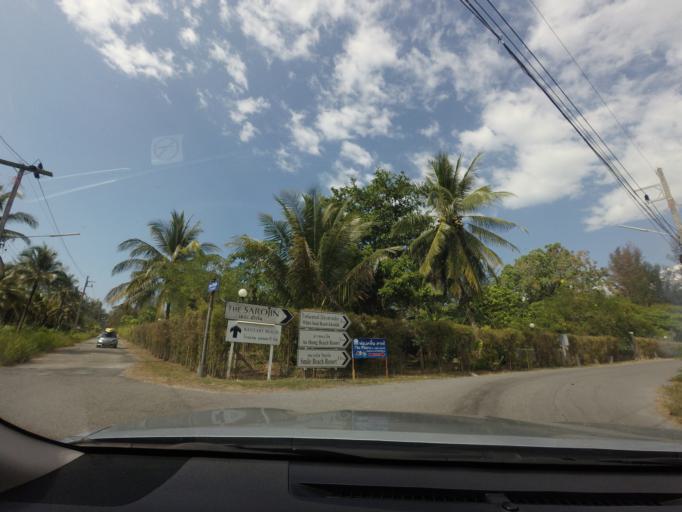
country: TH
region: Phangnga
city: Ban Khao Lak
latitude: 8.7295
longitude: 98.2399
